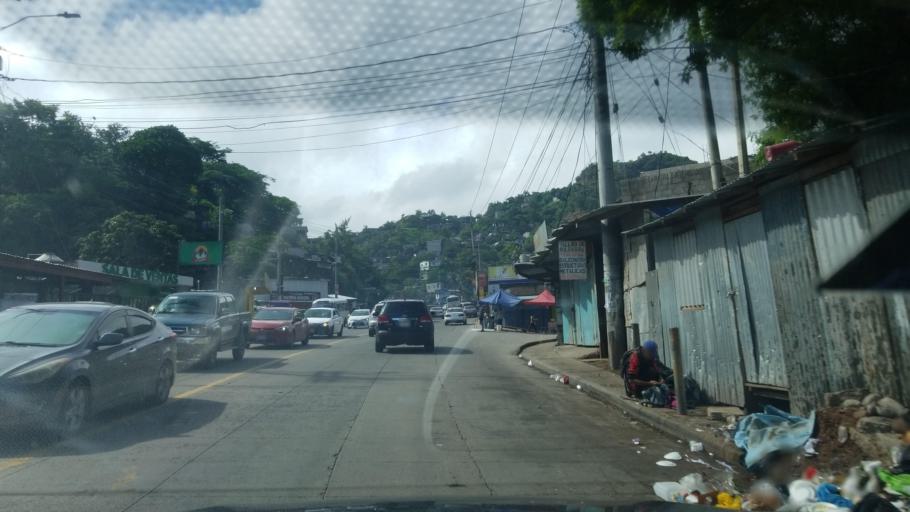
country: HN
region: Francisco Morazan
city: El Tablon
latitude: 14.0595
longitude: -87.1628
